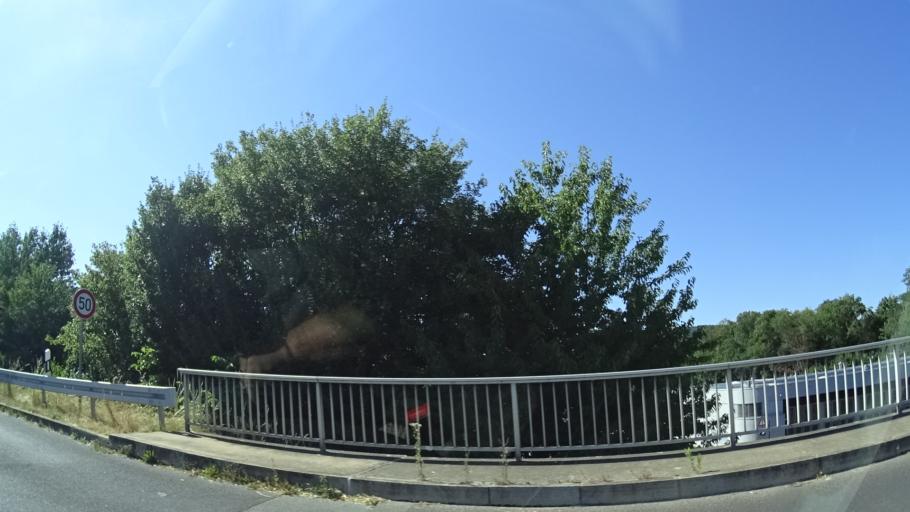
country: DE
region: Bavaria
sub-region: Regierungsbezirk Unterfranken
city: Kleinheubach
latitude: 49.7151
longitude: 9.2202
